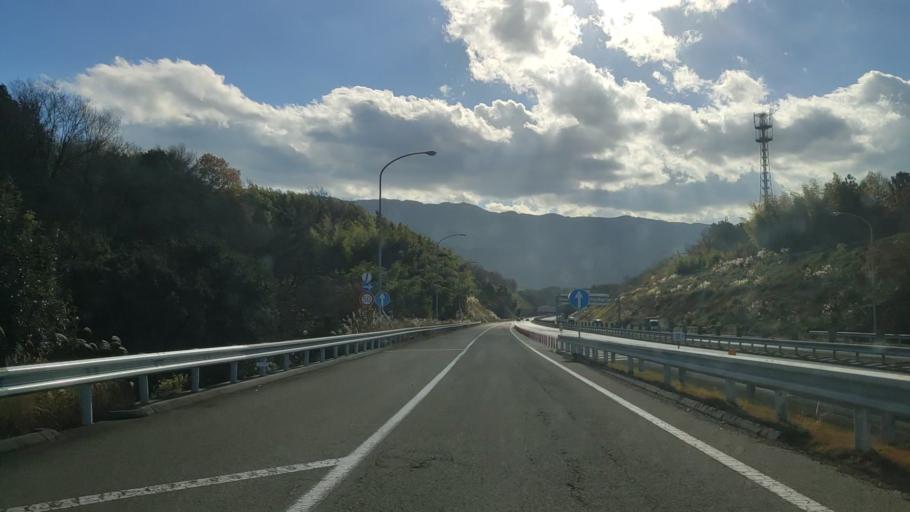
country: JP
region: Ehime
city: Kawanoecho
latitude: 33.9992
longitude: 133.5968
